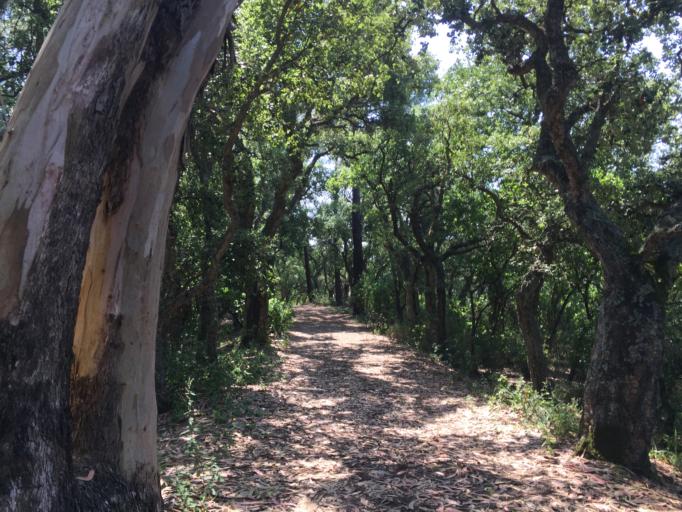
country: PT
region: Lisbon
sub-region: Mafra
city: Milharado
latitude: 38.9044
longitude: -9.1839
